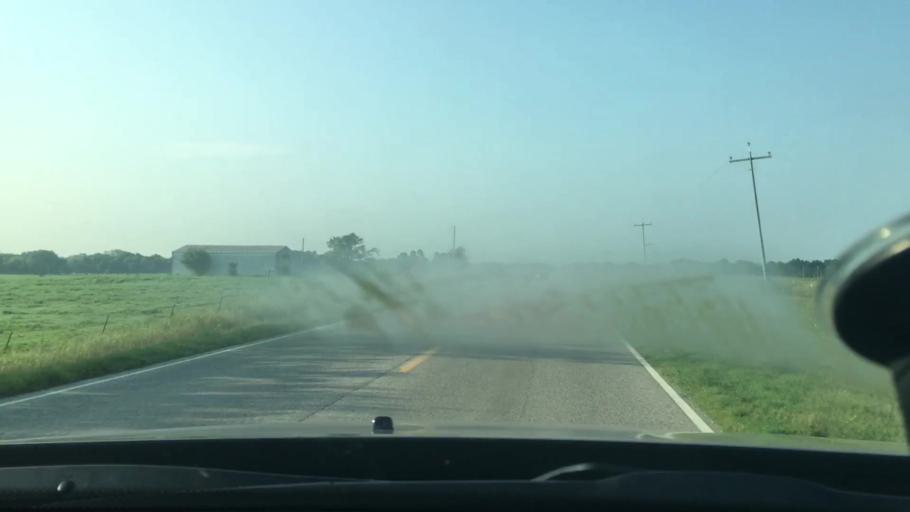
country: US
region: Oklahoma
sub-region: Pontotoc County
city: Ada
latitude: 34.7214
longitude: -96.6357
